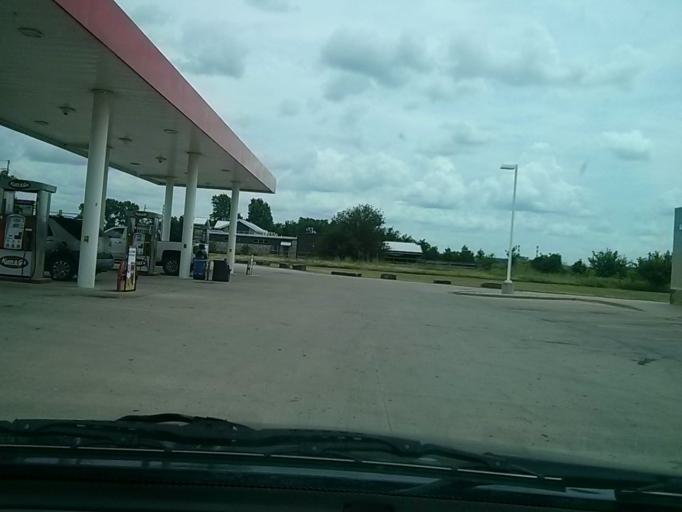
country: US
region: Oklahoma
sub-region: Tulsa County
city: Jenks
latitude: 36.0184
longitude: -95.9497
